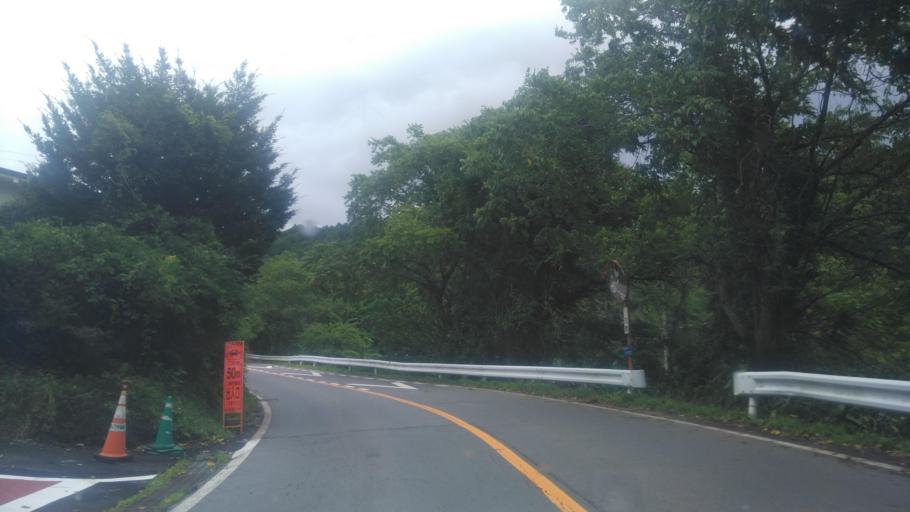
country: JP
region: Nagano
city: Ueda
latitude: 36.4891
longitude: 138.3721
